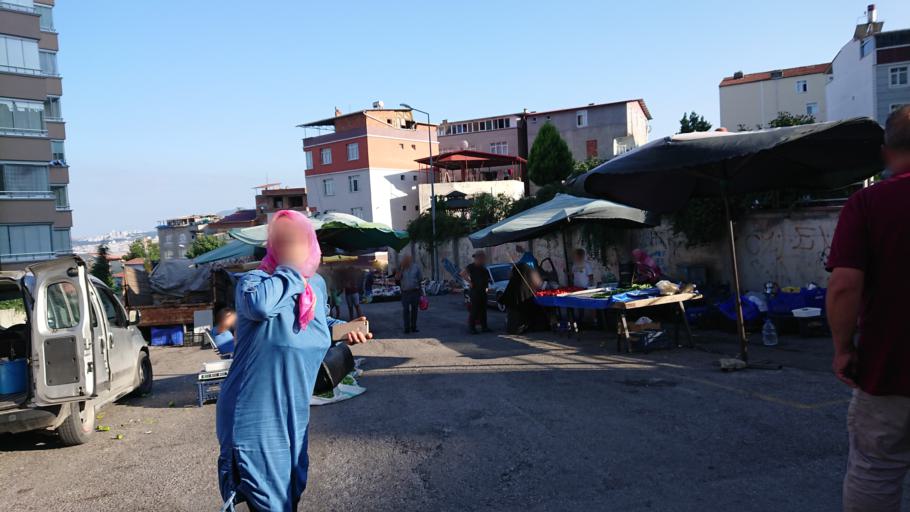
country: TR
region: Samsun
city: Samsun
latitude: 41.3002
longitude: 36.3209
